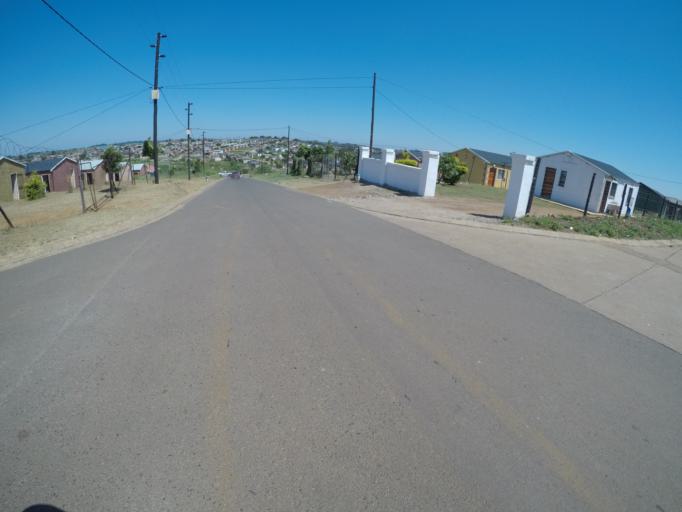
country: ZA
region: KwaZulu-Natal
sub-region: uThungulu District Municipality
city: Empangeni
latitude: -28.7641
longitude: 31.8768
